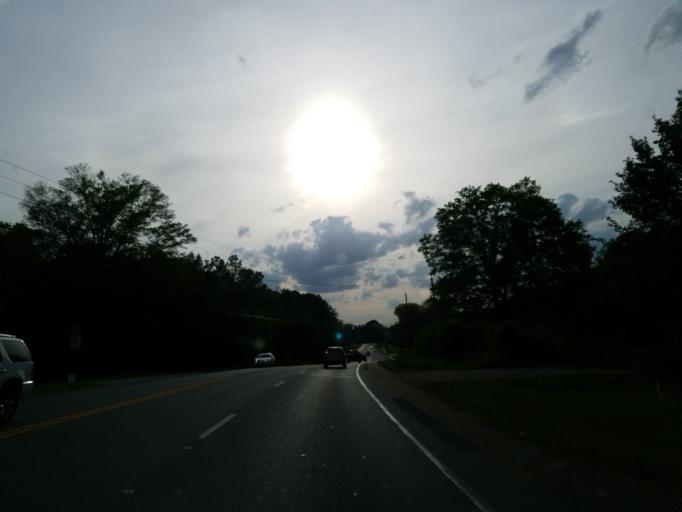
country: US
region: Georgia
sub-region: Cherokee County
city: Ball Ground
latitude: 34.2413
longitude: -84.3866
